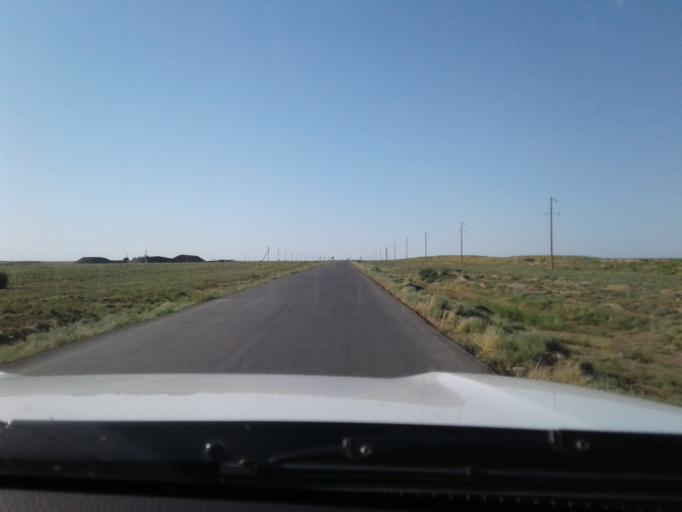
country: IR
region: Razavi Khorasan
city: Kalat-e Naderi
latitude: 37.1706
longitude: 60.0462
